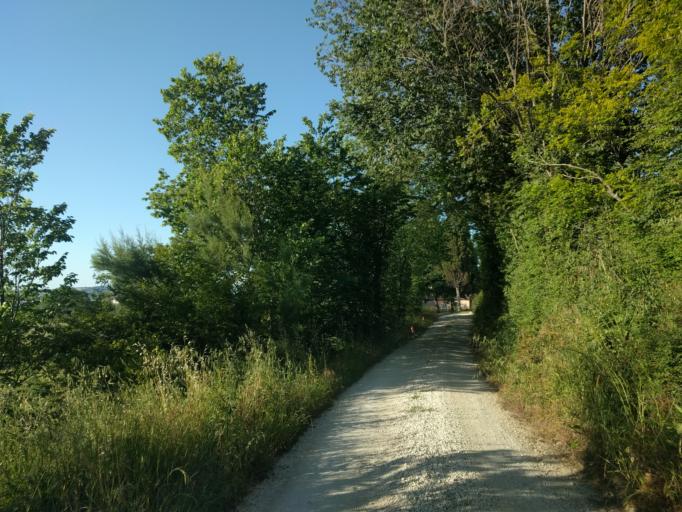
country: IT
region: The Marches
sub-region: Provincia di Pesaro e Urbino
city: Montemaggiore al Metauro
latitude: 43.7449
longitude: 12.9529
